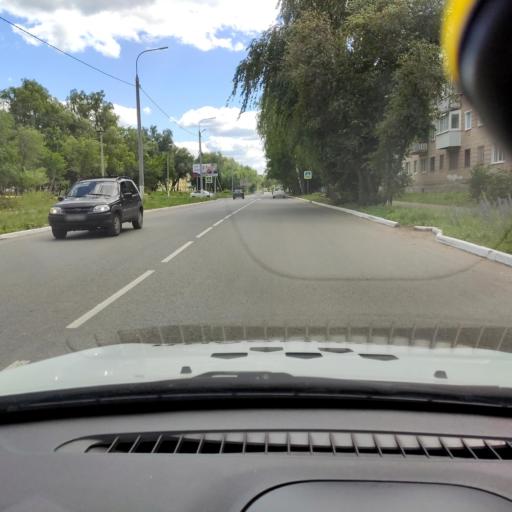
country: RU
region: Samara
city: Zhigulevsk
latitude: 53.4023
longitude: 49.5105
